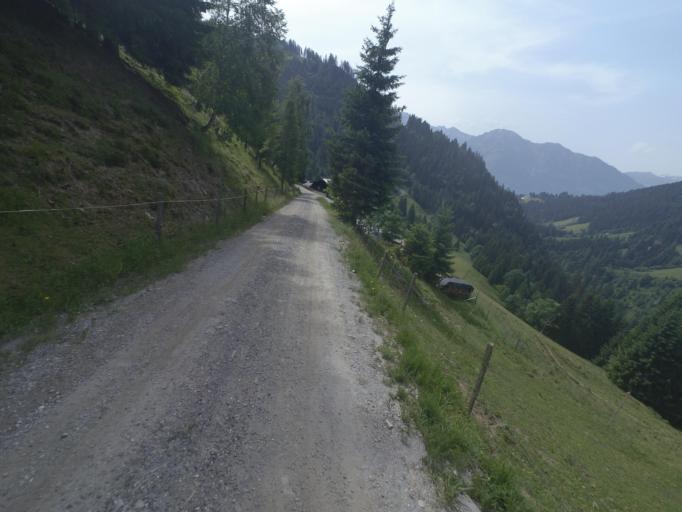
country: AT
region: Salzburg
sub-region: Politischer Bezirk Sankt Johann im Pongau
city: Muhlbach am Hochkonig
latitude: 47.3578
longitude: 13.1143
